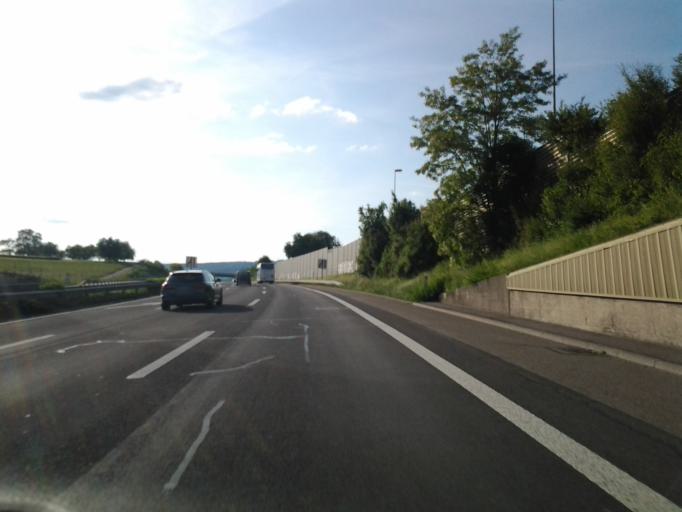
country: CH
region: Lucerne
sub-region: Sursee District
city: Knutwil
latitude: 47.1923
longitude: 8.0746
